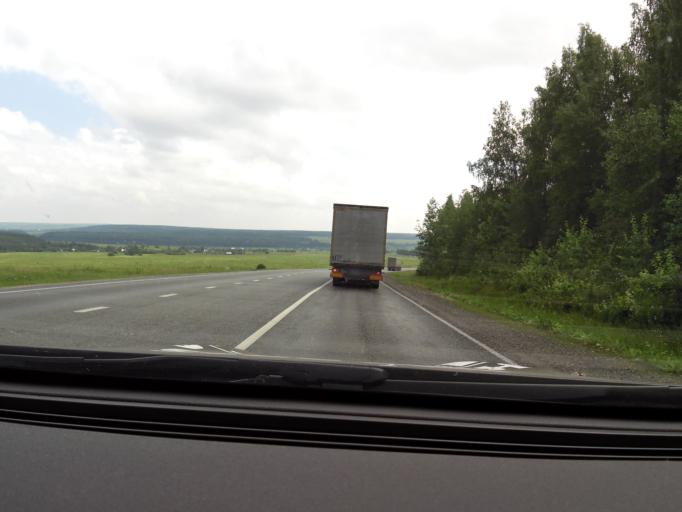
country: RU
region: Perm
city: Suksun
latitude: 57.0821
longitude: 57.4054
